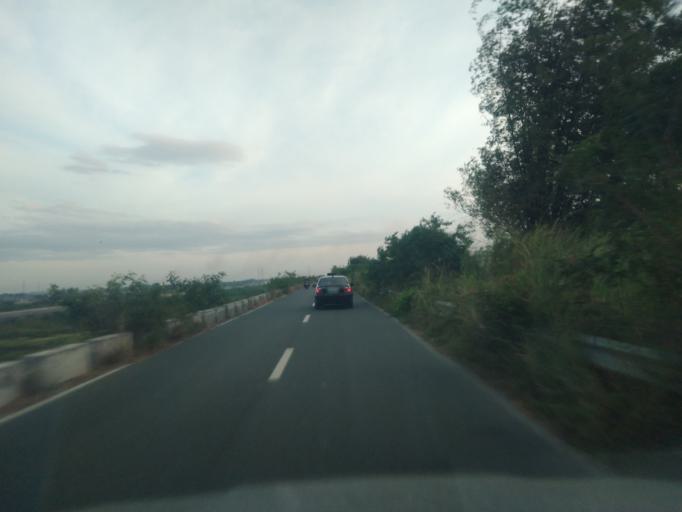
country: PH
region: Central Luzon
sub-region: Province of Pampanga
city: Santa Rita
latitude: 15.0098
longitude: 120.6283
